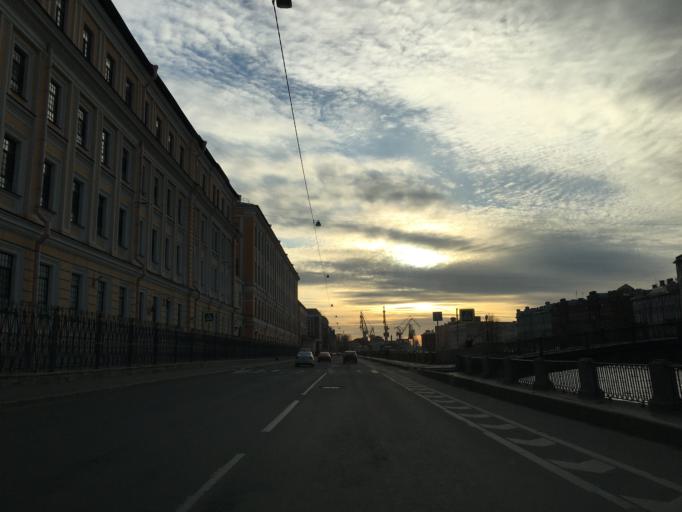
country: RU
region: St.-Petersburg
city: Admiralteisky
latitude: 59.9156
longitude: 30.2919
